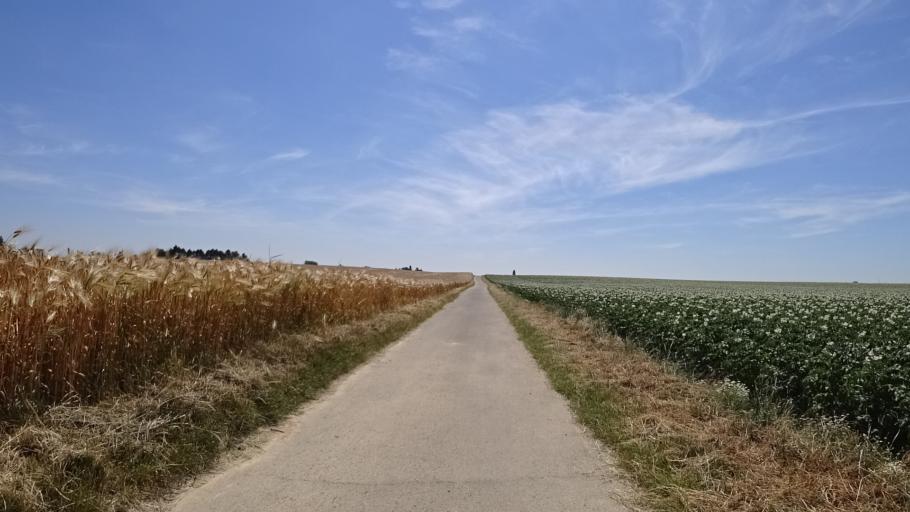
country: BE
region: Wallonia
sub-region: Province de Namur
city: Gembloux
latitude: 50.5746
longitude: 4.6793
